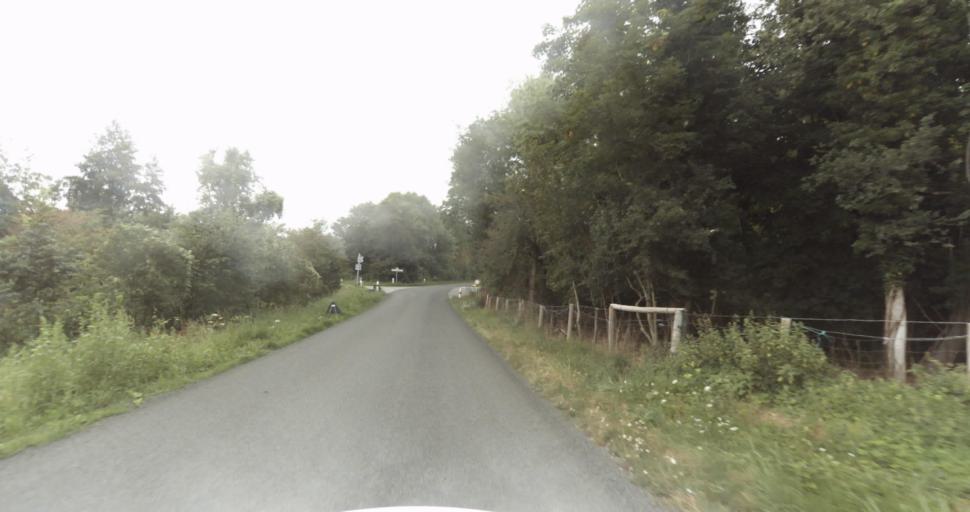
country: FR
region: Centre
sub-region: Departement d'Eure-et-Loir
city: Vert-en-Drouais
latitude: 48.7647
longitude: 1.3148
